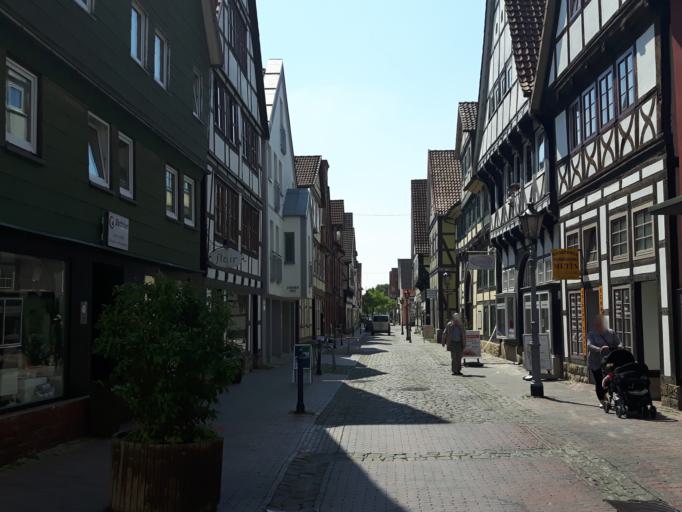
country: DE
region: Lower Saxony
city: Rinteln
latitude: 52.1867
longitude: 9.0809
